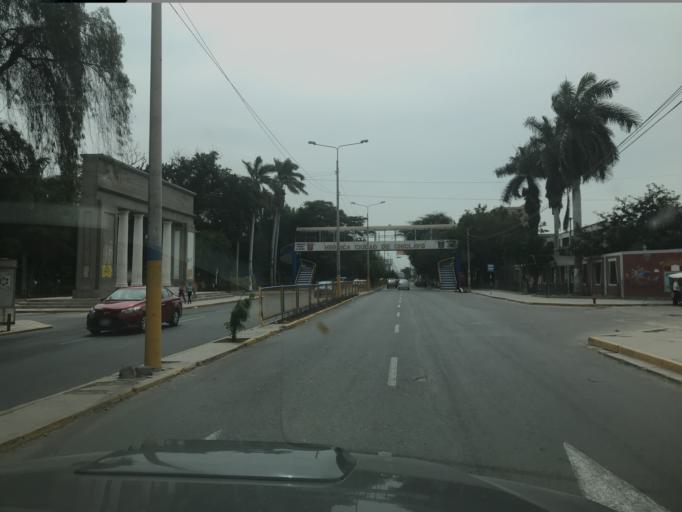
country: PE
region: Lambayeque
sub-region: Provincia de Chiclayo
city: Chiclayo
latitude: -6.7711
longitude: -79.8464
